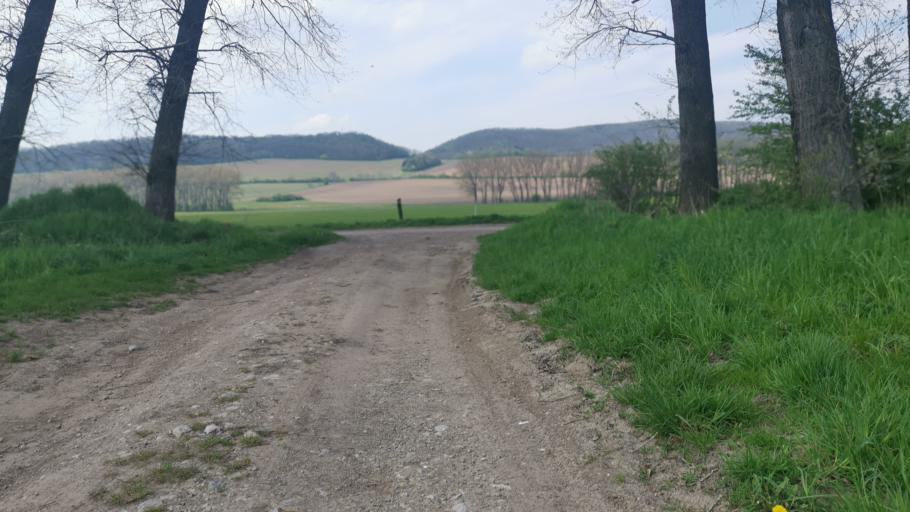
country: SK
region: Trnavsky
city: Smolenice
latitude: 48.5357
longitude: 17.3793
